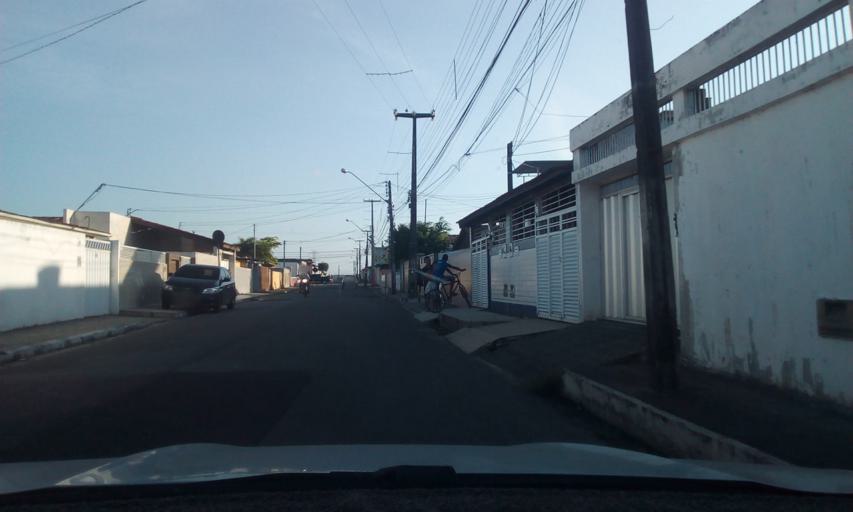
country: BR
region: Paraiba
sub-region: Bayeux
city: Bayeux
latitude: -7.1793
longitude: -34.8956
